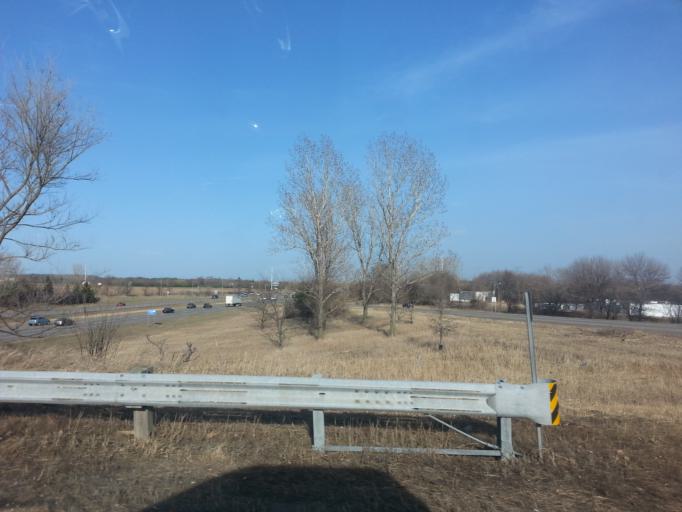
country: US
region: Minnesota
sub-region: Washington County
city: Lake Elmo
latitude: 44.9478
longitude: -92.8624
